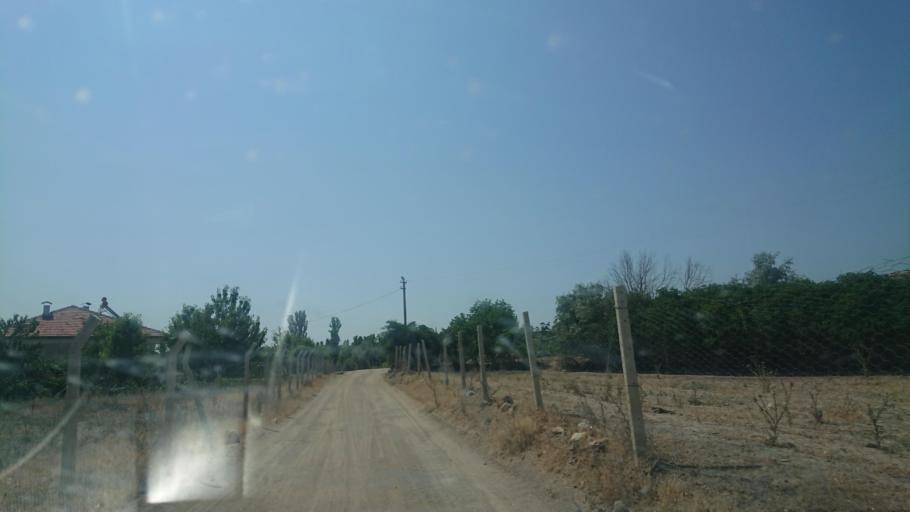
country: TR
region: Aksaray
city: Agacoren
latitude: 38.9349
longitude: 33.9513
